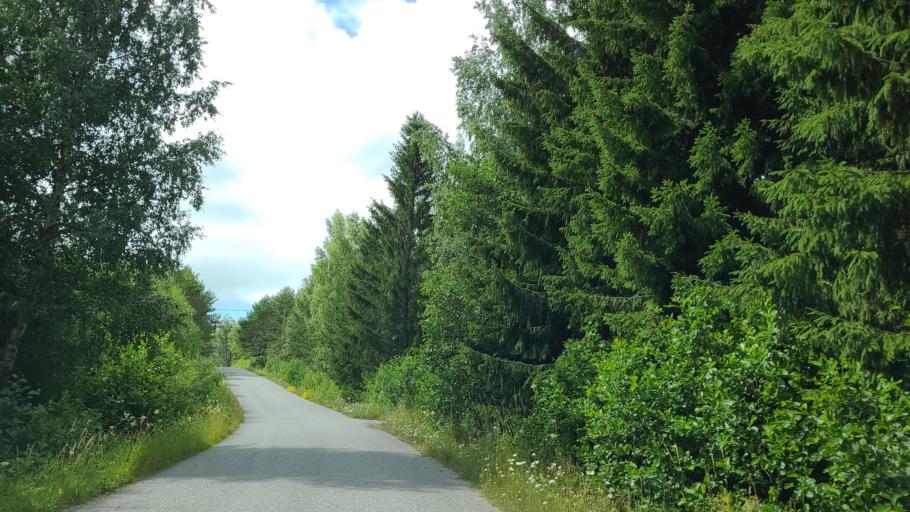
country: FI
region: Varsinais-Suomi
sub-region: Aboland-Turunmaa
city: Nagu
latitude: 60.1639
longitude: 22.0248
